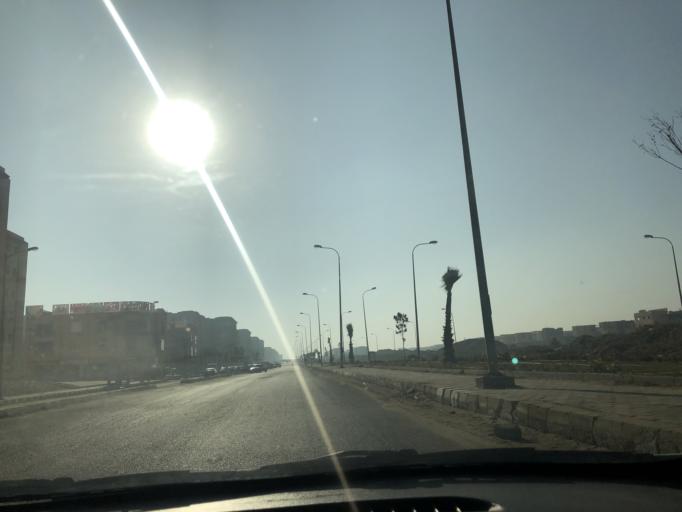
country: EG
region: Al Jizah
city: Madinat Sittah Uktubar
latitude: 29.9251
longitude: 31.0317
